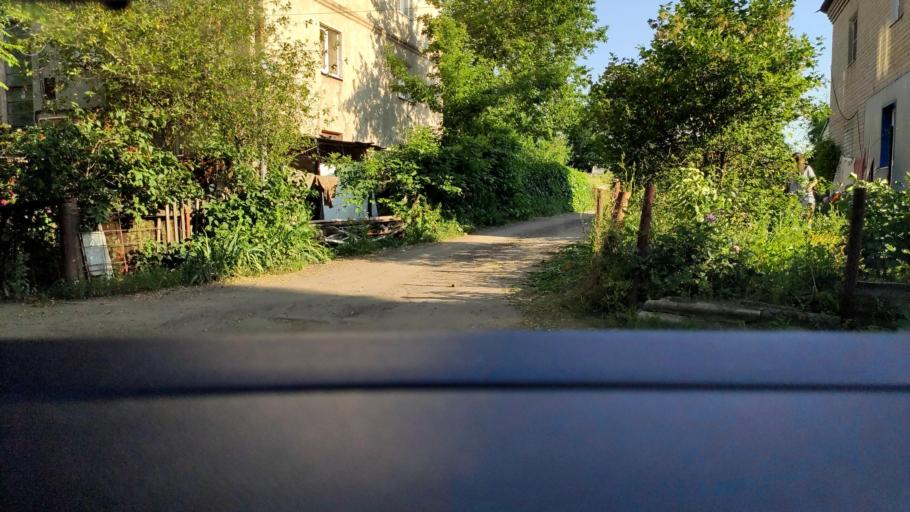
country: RU
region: Voronezj
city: Voronezh
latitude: 51.6242
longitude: 39.1779
